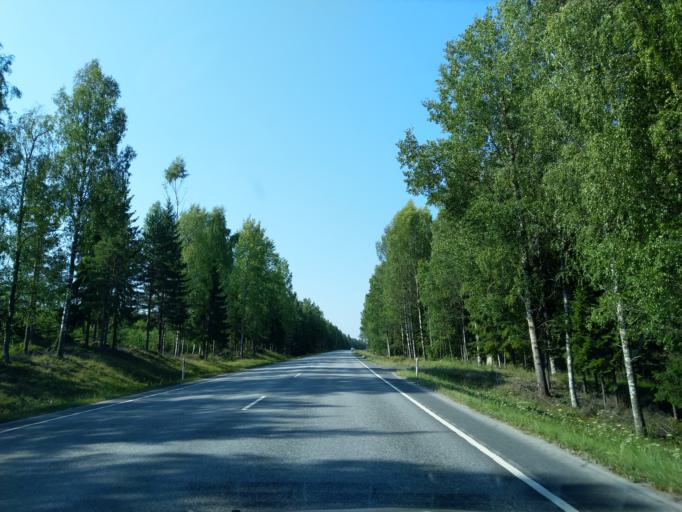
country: FI
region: Satakunta
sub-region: Pori
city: Pomarkku
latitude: 61.6388
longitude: 21.9433
